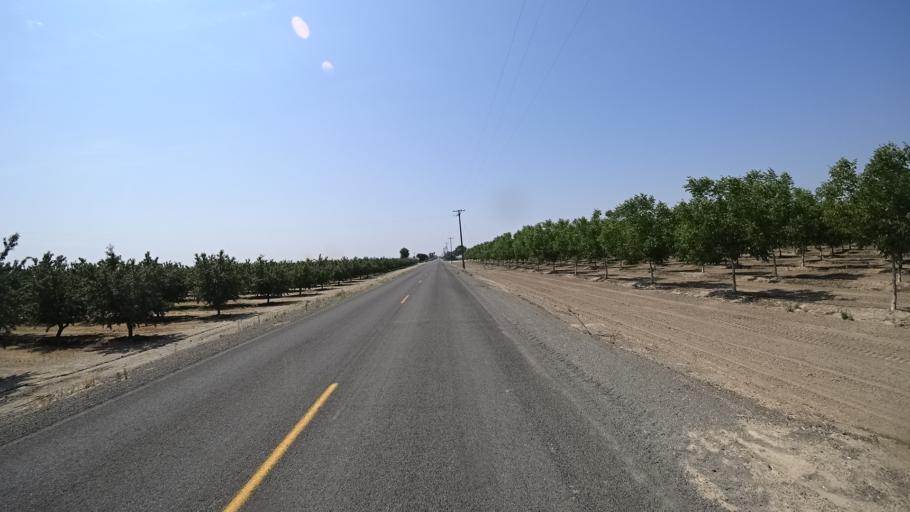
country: US
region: California
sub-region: Fresno County
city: Laton
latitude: 36.3912
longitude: -119.7450
